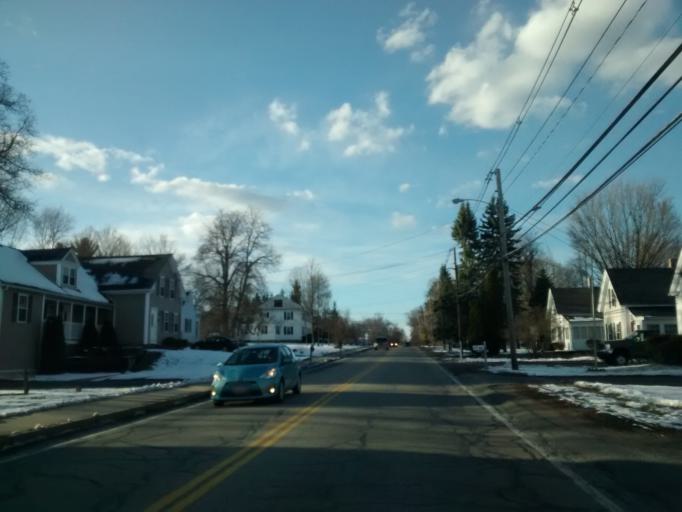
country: US
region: Massachusetts
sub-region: Middlesex County
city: Hopkinton
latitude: 42.2110
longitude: -71.5137
